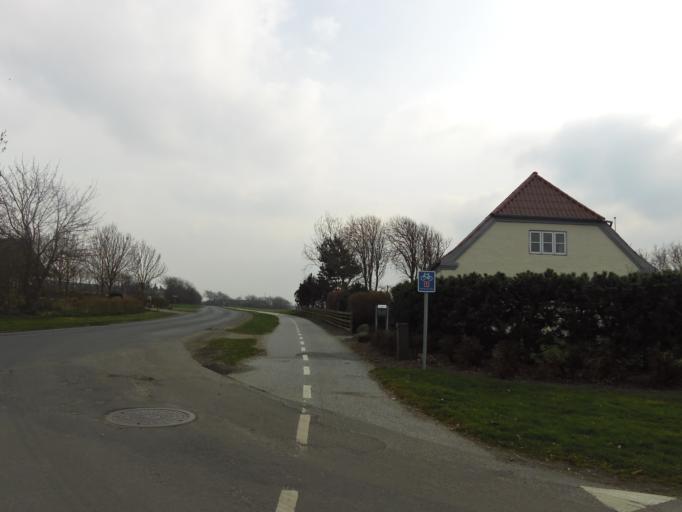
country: DK
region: South Denmark
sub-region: Esbjerg Kommune
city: Ribe
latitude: 55.3525
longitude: 8.7441
